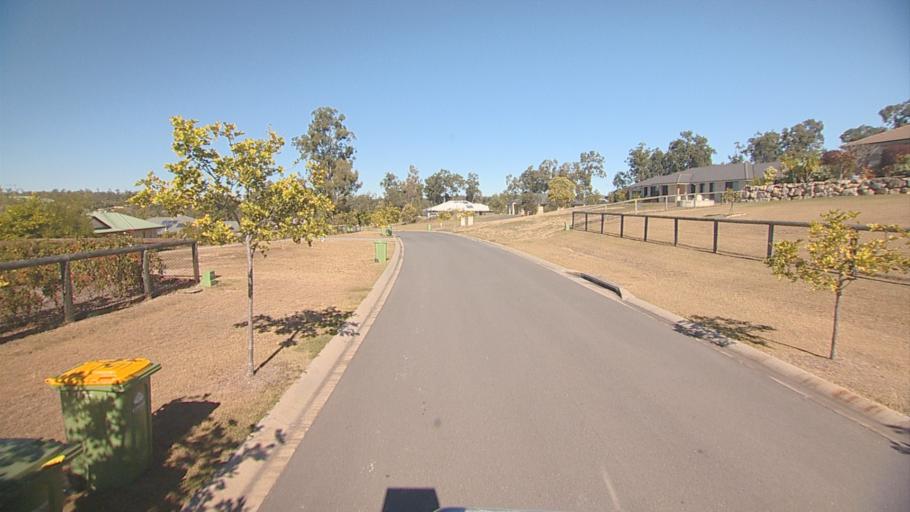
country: AU
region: Queensland
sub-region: Logan
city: North Maclean
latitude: -27.7507
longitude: 152.9503
